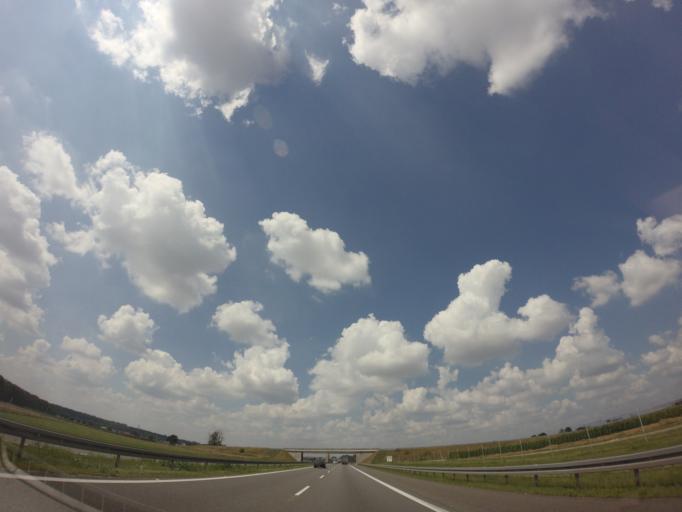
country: PL
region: Opole Voivodeship
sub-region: Powiat strzelecki
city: Strzelce Opolskie
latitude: 50.4552
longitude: 18.2938
